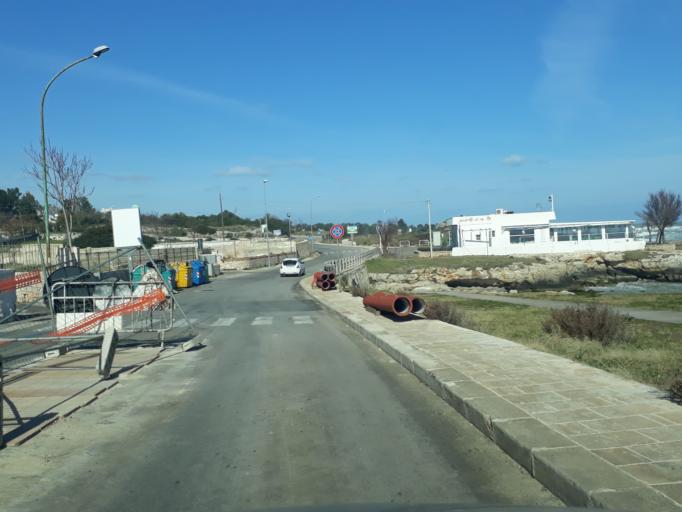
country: IT
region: Apulia
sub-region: Provincia di Bari
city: Monopoli
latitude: 40.9076
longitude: 17.3475
